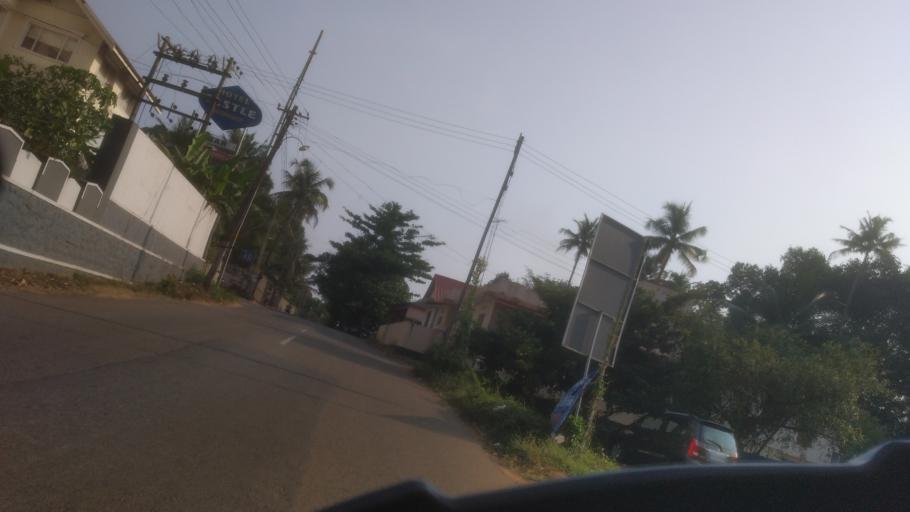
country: IN
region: Kerala
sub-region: Ernakulam
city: Piravam
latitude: 9.8231
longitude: 76.5020
